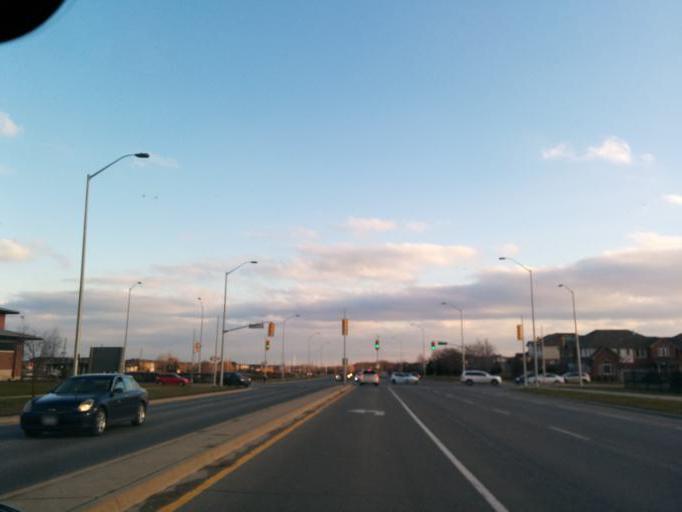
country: CA
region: Ontario
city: Burlington
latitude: 43.4328
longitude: -79.7749
